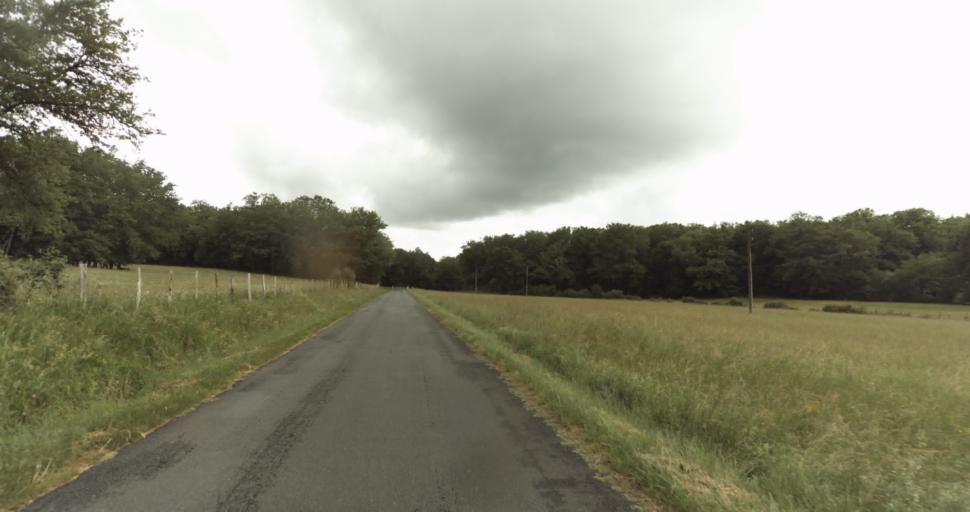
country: FR
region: Aquitaine
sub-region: Departement de la Dordogne
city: Belves
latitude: 44.7542
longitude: 0.9528
